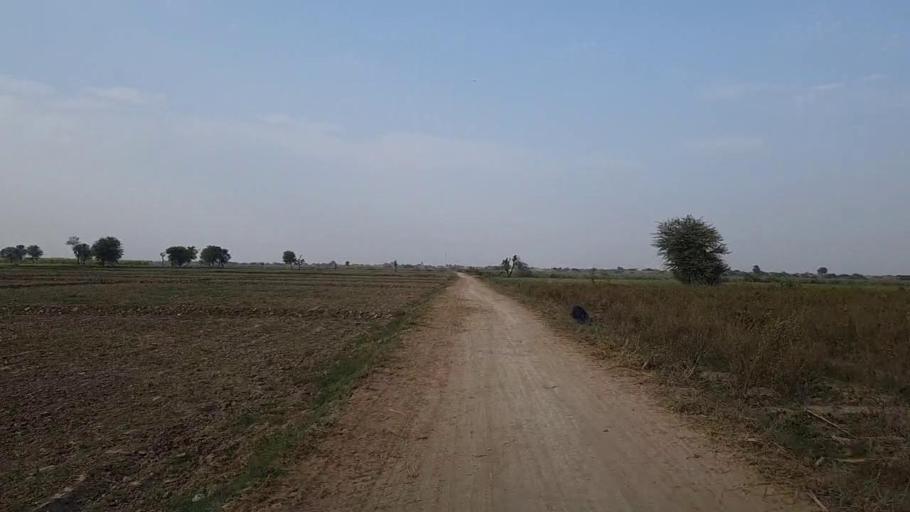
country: PK
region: Sindh
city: Pithoro
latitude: 25.4349
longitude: 69.2370
